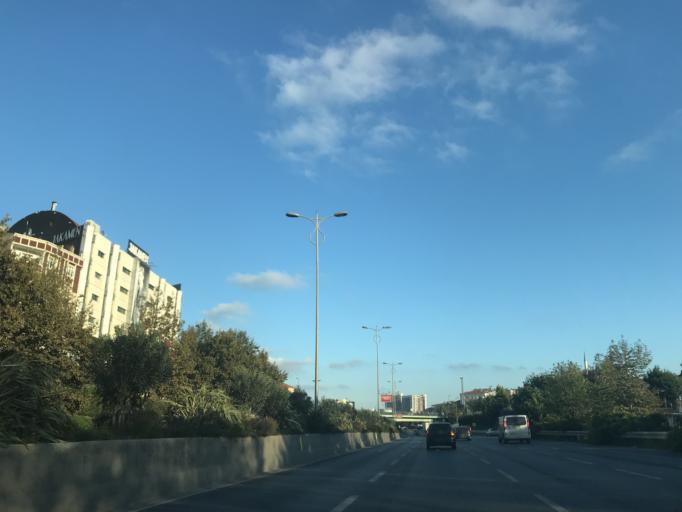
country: TR
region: Istanbul
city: Esenler
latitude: 41.0490
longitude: 28.8749
